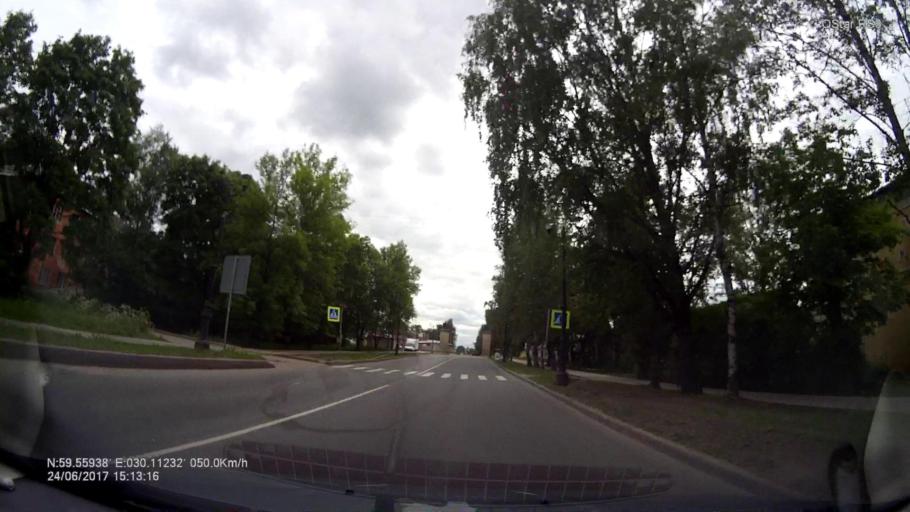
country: RU
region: Leningrad
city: Gatchina
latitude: 59.5592
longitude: 30.1121
